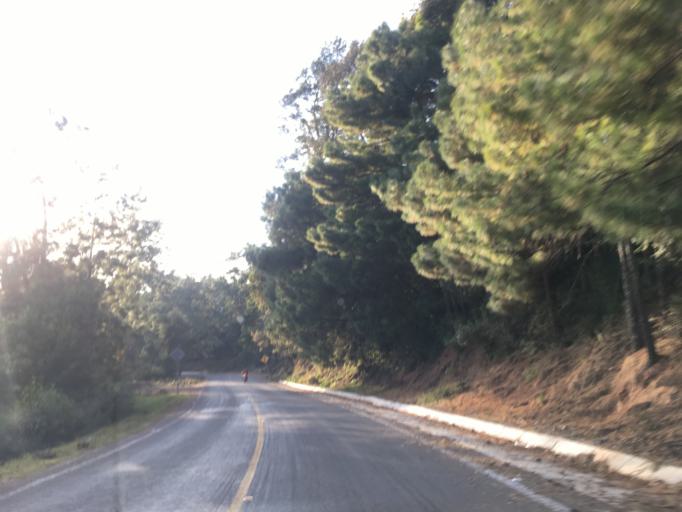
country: MX
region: Michoacan
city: Tzitzio
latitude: 19.6835
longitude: -100.8978
